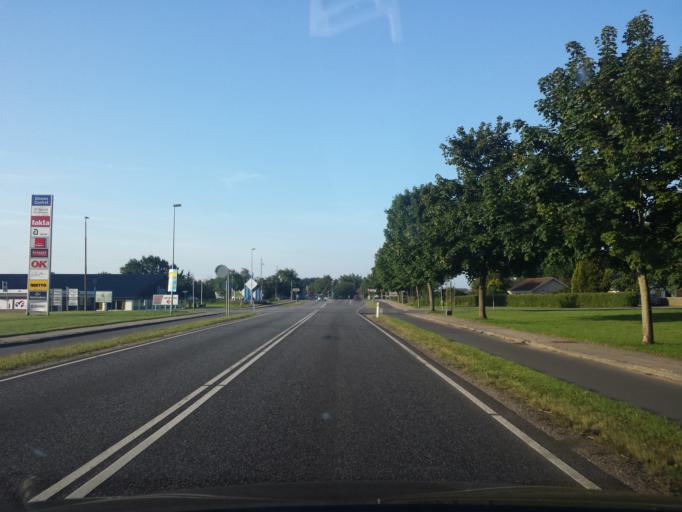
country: DK
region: South Denmark
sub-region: Sonderborg Kommune
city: Grasten
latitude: 54.9108
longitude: 9.5874
